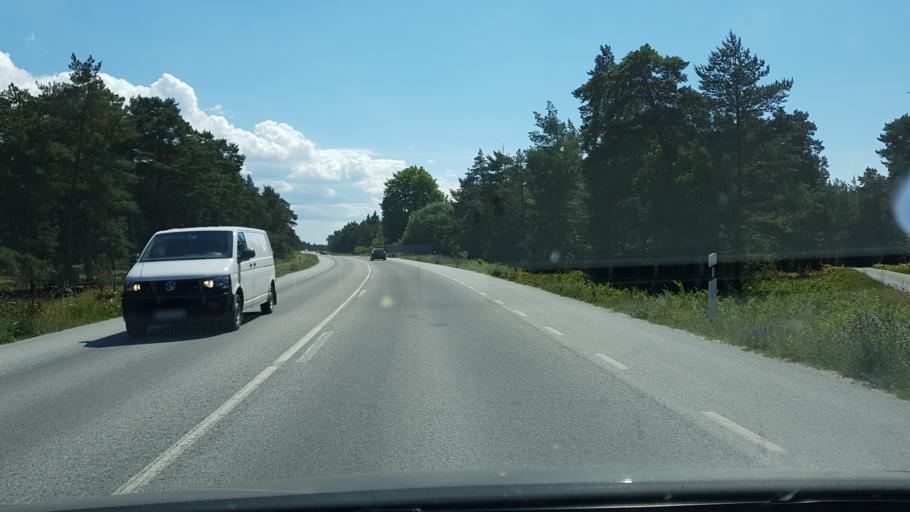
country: SE
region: Gotland
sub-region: Gotland
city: Vibble
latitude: 57.5595
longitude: 18.2021
